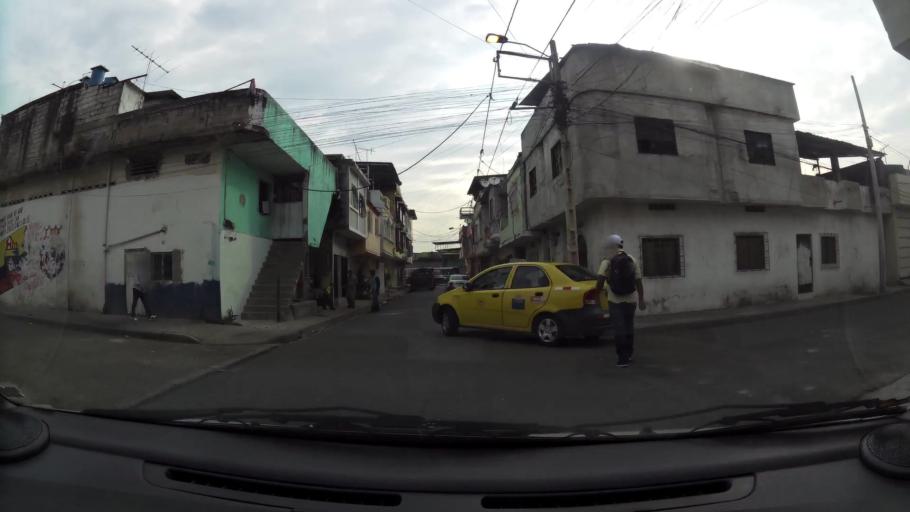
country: EC
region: Guayas
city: Guayaquil
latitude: -2.2516
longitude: -79.8983
